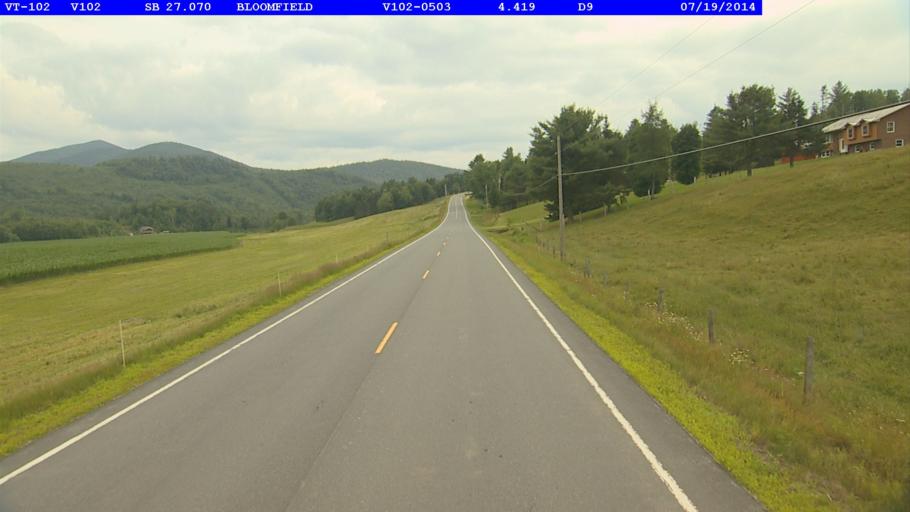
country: US
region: New Hampshire
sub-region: Coos County
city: Colebrook
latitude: 44.7947
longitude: -71.5769
